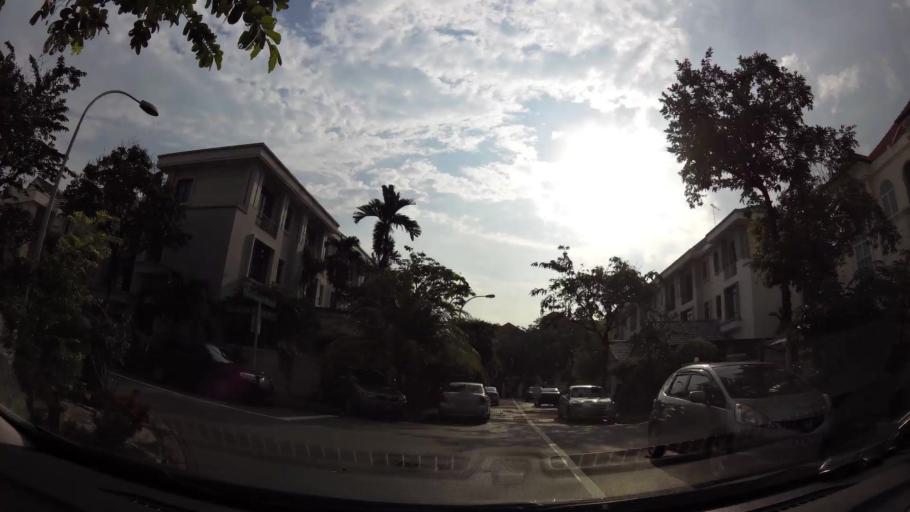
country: SG
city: Singapore
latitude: 1.3227
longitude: 103.9559
